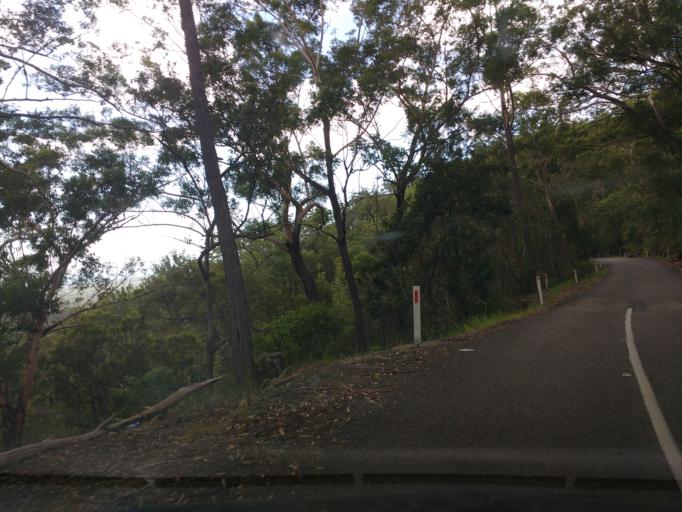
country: AU
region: Queensland
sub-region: Hinchinbrook
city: Ingham
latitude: -19.0083
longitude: 146.2782
